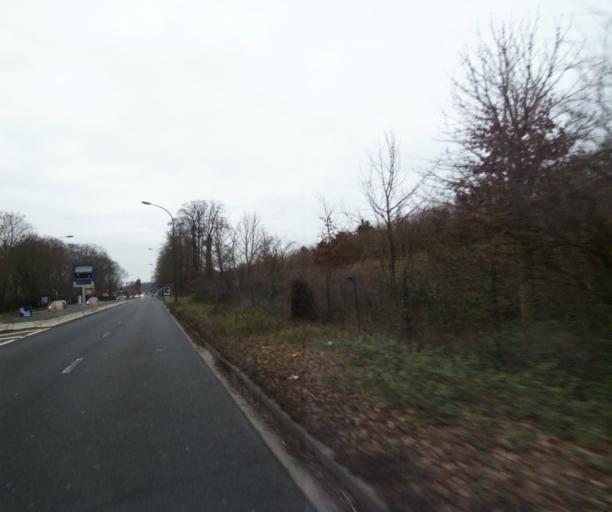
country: FR
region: Ile-de-France
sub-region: Departement des Hauts-de-Seine
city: Vaucresson
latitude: 48.8329
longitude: 2.1483
